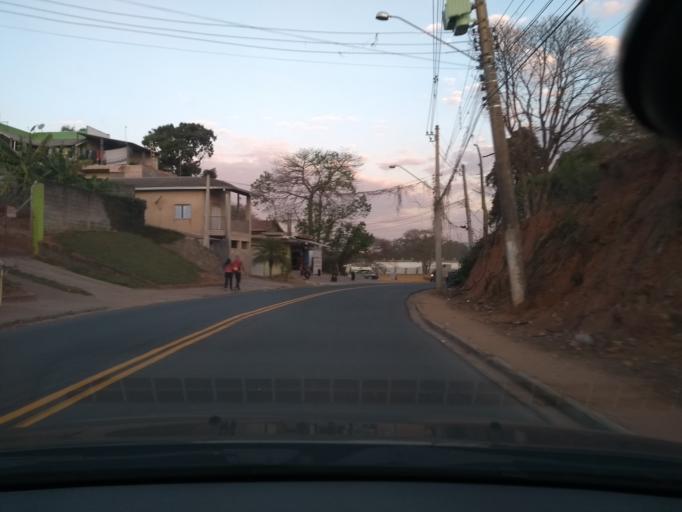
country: BR
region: Sao Paulo
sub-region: Itupeva
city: Itupeva
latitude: -23.1424
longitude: -47.0362
